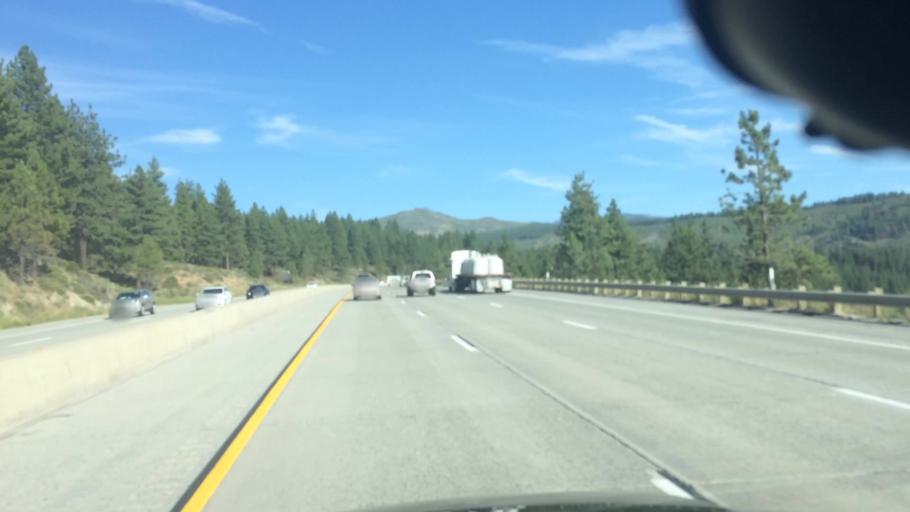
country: US
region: California
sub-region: Nevada County
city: Truckee
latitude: 39.3816
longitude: -120.0761
